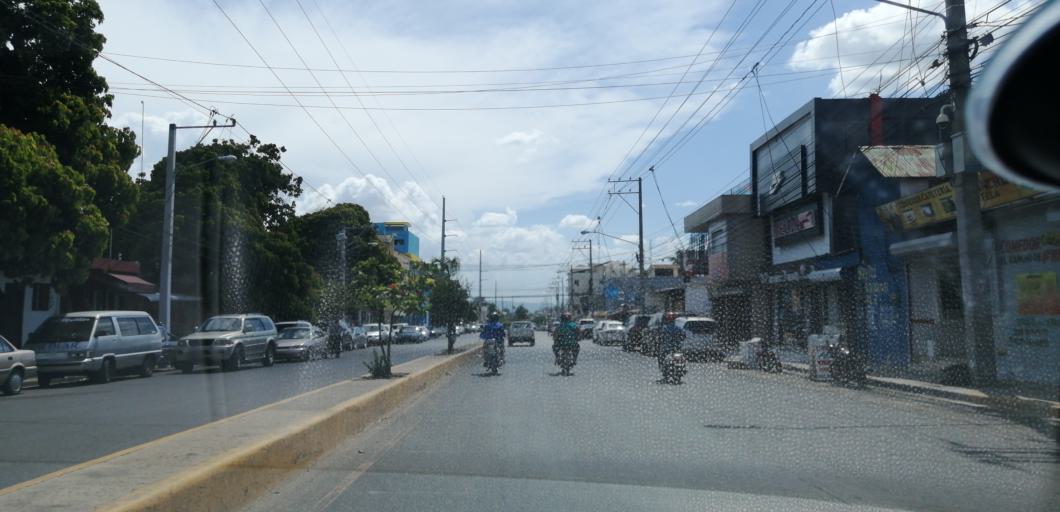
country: DO
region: Santiago
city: Santiago de los Caballeros
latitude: 19.4871
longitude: -70.7230
